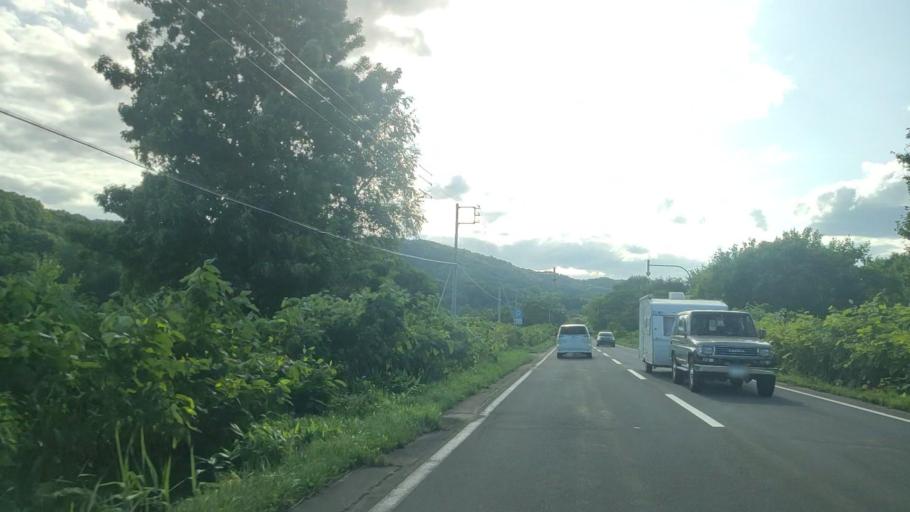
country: JP
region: Hokkaido
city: Nayoro
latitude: 44.7291
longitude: 142.0692
